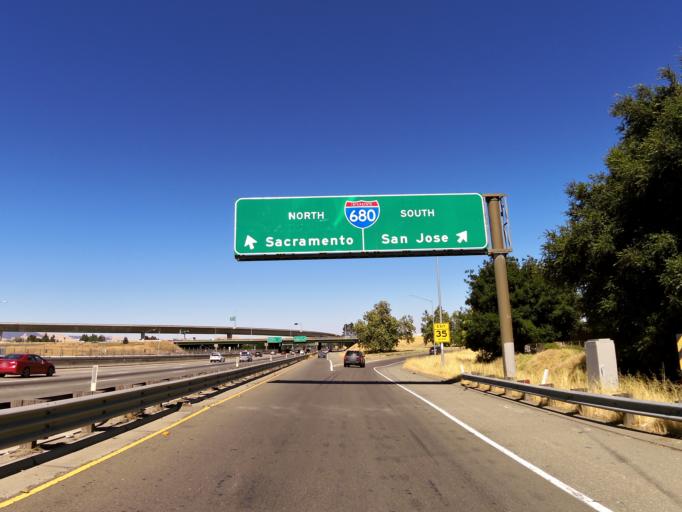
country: US
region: California
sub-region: Alameda County
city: Dublin
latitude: 37.7000
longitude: -121.9257
